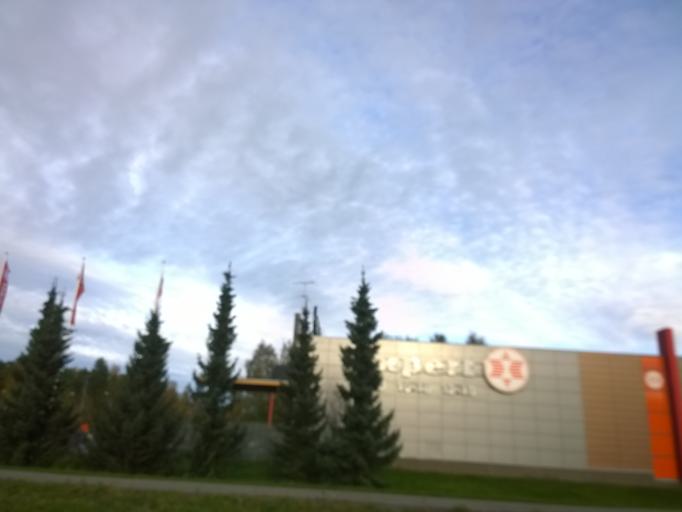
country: FI
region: Pirkanmaa
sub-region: Tampere
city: Tampere
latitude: 61.4925
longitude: 23.8230
